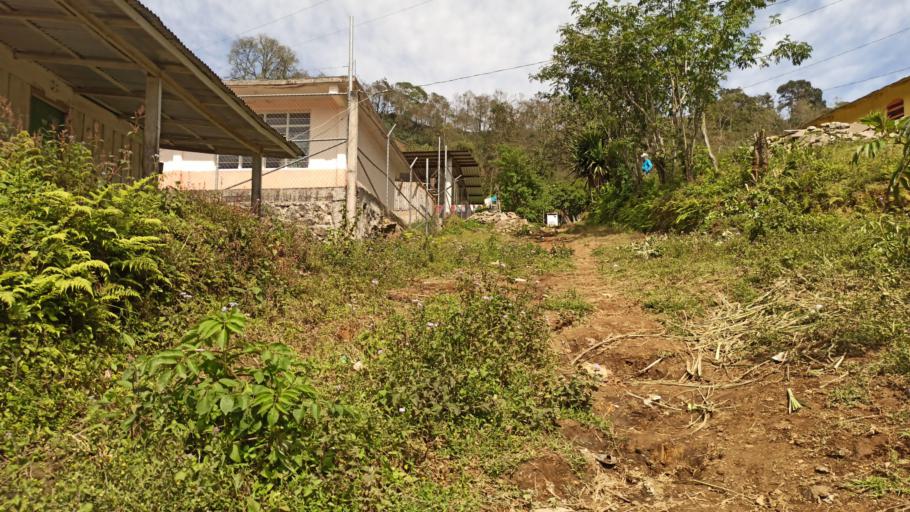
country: MX
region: Veracruz
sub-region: La Perla
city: Metlac Hernandez (Metlac Primero)
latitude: 18.9691
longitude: -97.1024
